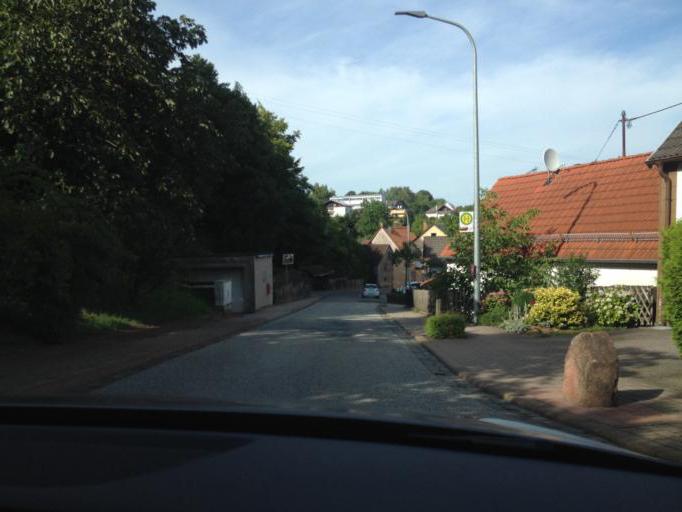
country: DE
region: Rheinland-Pfalz
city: Dunzweiler
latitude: 49.4136
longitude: 7.3020
